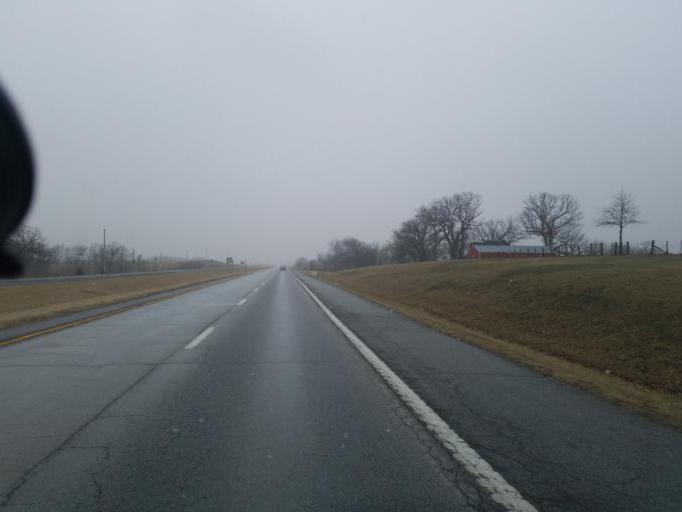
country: US
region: Missouri
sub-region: Macon County
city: La Plata
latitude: 39.9713
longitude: -92.4766
